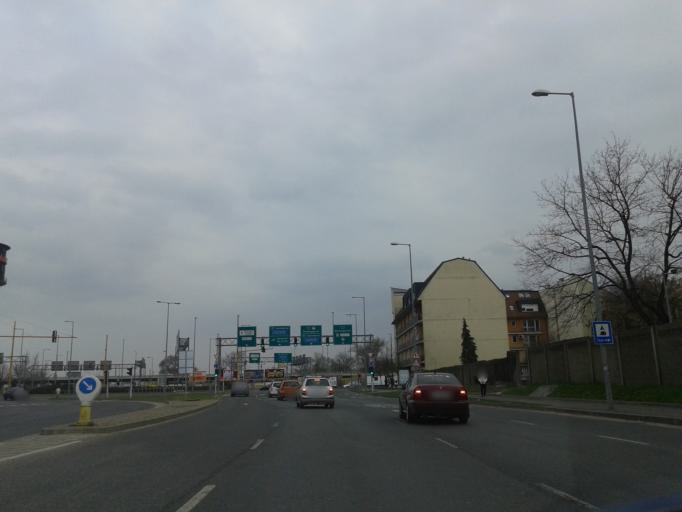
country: HU
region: Gyor-Moson-Sopron
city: Gyor
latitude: 47.6894
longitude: 17.6434
